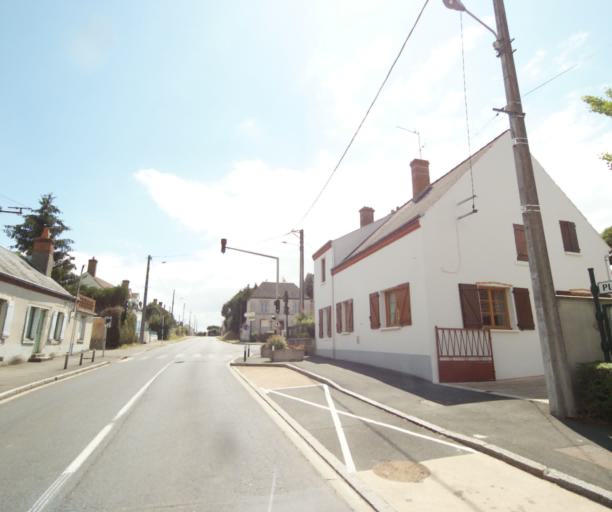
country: FR
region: Centre
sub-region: Departement du Loiret
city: Mardie
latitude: 47.8908
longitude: 2.0550
